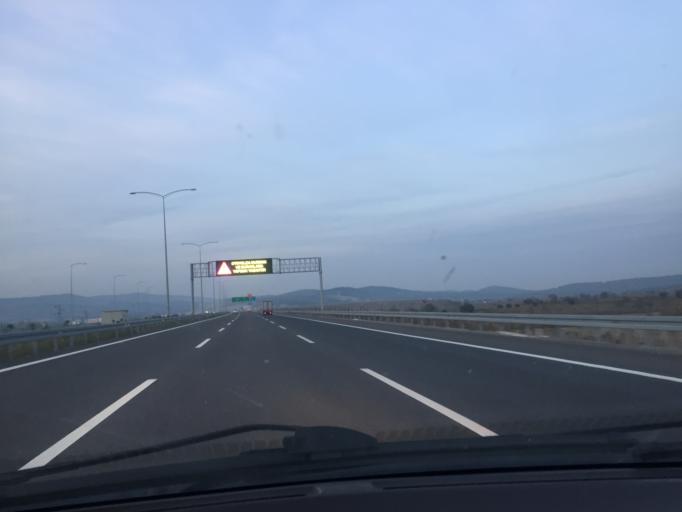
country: TR
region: Manisa
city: Halitpasa
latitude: 38.7608
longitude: 27.6603
